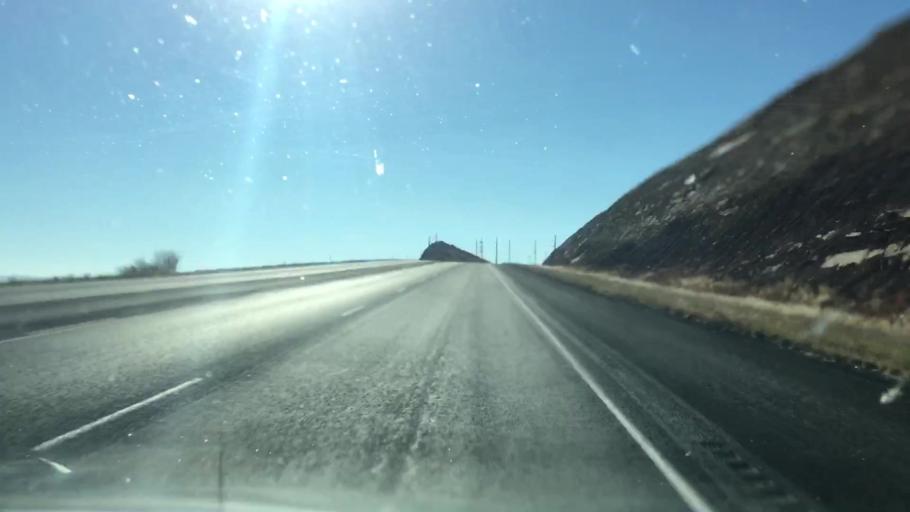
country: US
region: Utah
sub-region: Washington County
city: Washington
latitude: 37.1647
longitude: -113.4224
